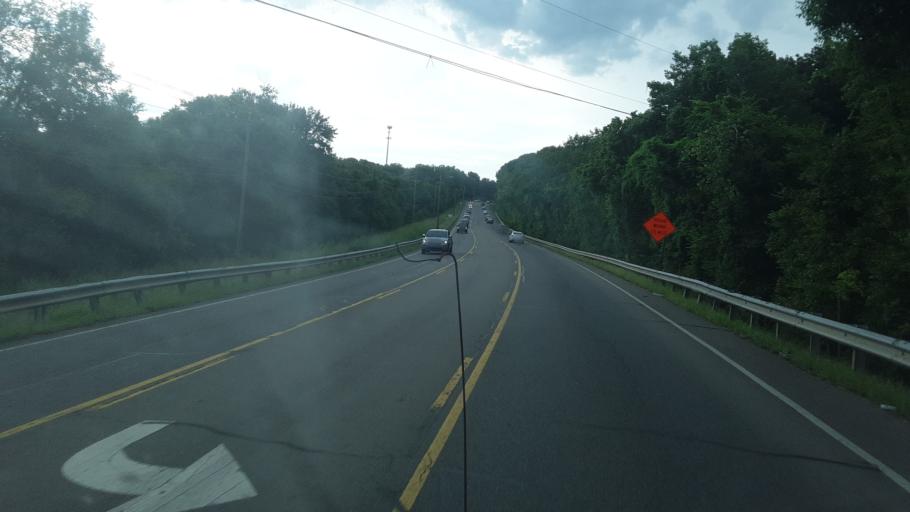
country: US
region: Tennessee
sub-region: Montgomery County
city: Clarksville
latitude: 36.5382
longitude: -87.2847
